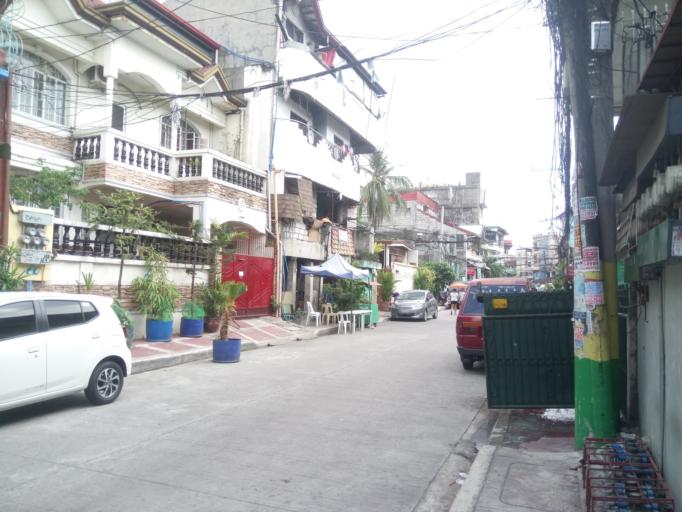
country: PH
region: Calabarzon
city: Bagong Pagasa
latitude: 14.6607
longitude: 121.0213
